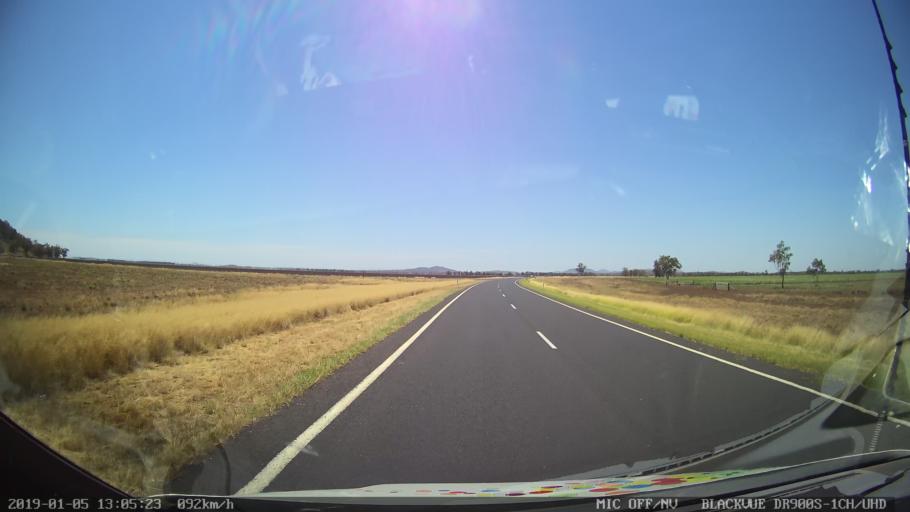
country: AU
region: New South Wales
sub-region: Gunnedah
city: Gunnedah
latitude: -31.0958
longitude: 149.8525
